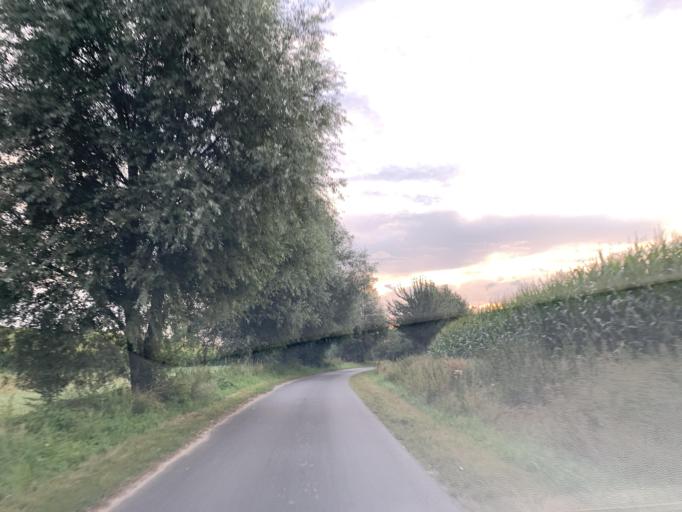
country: DE
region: Mecklenburg-Vorpommern
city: Blankensee
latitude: 53.4110
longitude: 13.2560
